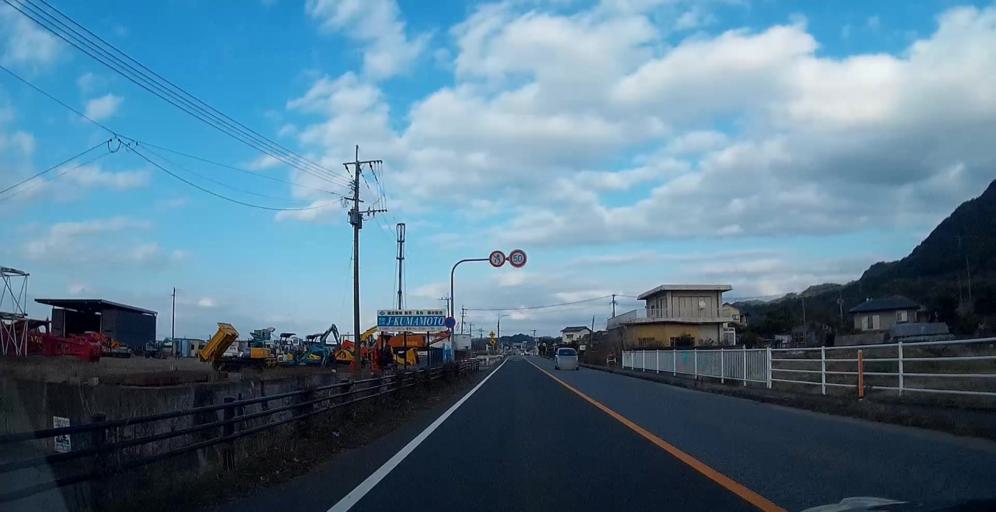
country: JP
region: Kumamoto
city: Yatsushiro
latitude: 32.5321
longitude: 130.6646
